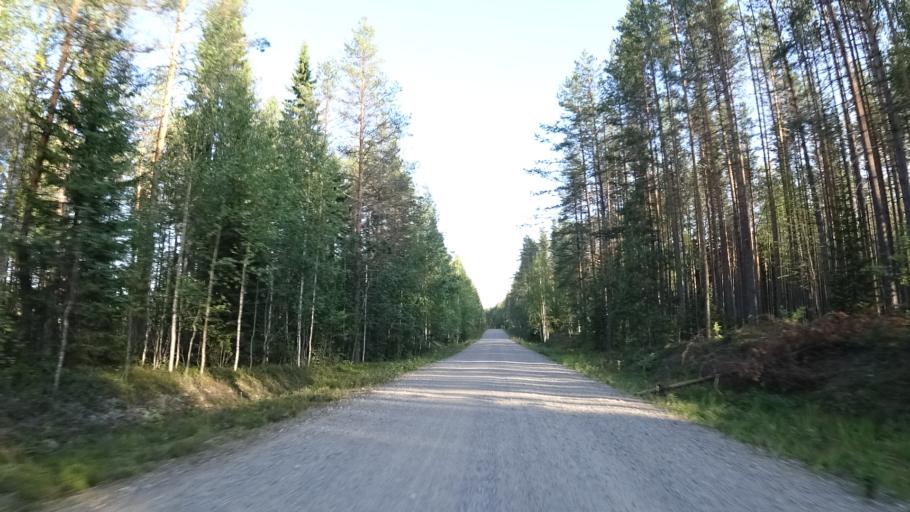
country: FI
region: North Karelia
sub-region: Joensuu
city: Ilomantsi
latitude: 63.1321
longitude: 30.7097
